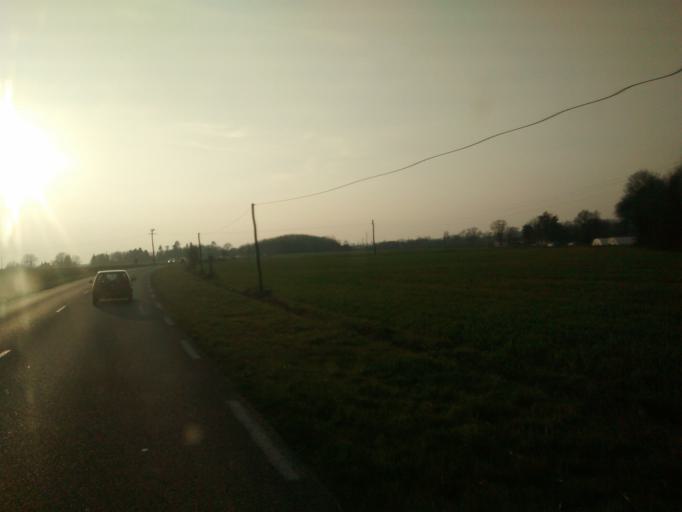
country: FR
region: Brittany
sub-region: Departement d'Ille-et-Vilaine
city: Chavagne
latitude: 48.0588
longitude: -1.7946
